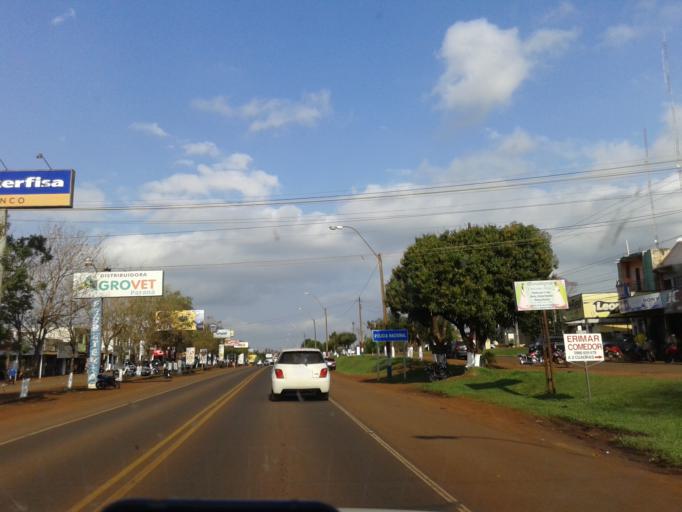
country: PY
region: Itapua
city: Arquitecto Tomas Romero Pereira
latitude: -26.5271
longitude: -55.2625
